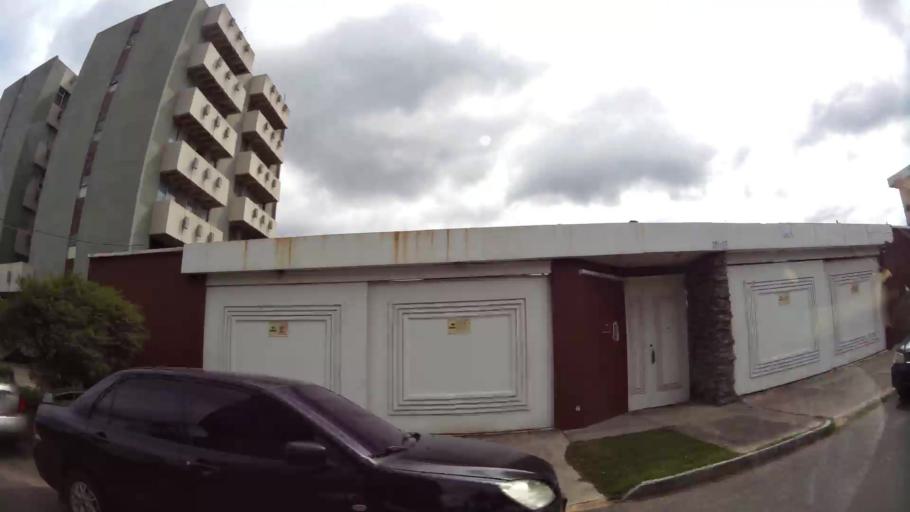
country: GT
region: Guatemala
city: Santa Catarina Pinula
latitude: 14.5789
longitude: -90.5243
